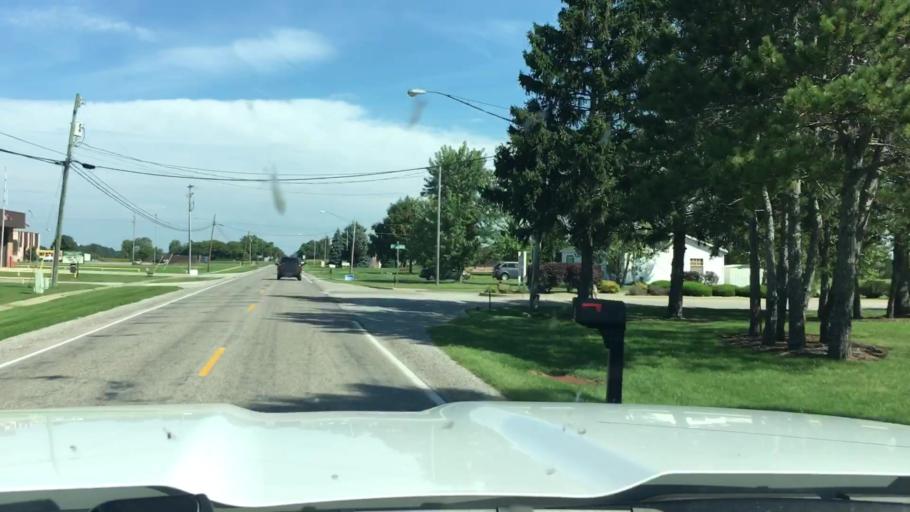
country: US
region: Michigan
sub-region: Saginaw County
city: Hemlock
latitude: 43.4224
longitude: -84.2298
